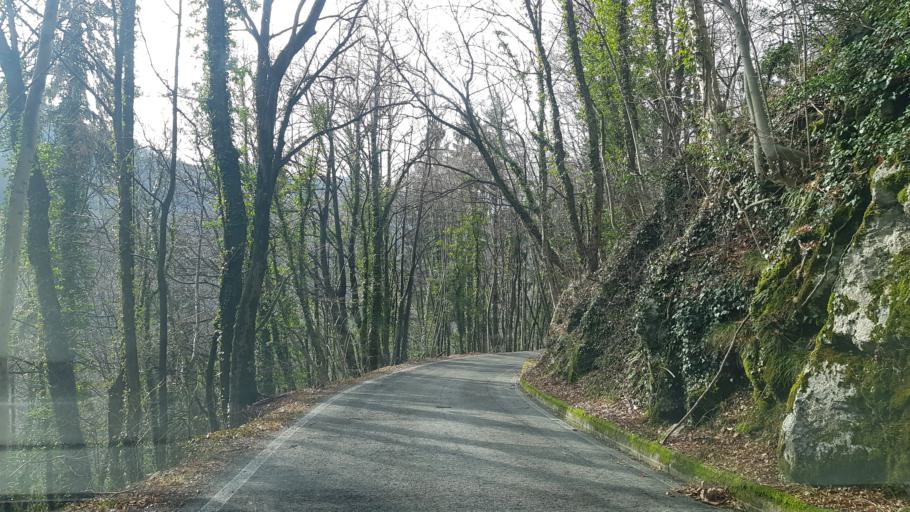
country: IT
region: Friuli Venezia Giulia
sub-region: Provincia di Udine
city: Clodig
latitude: 46.1781
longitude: 13.5748
